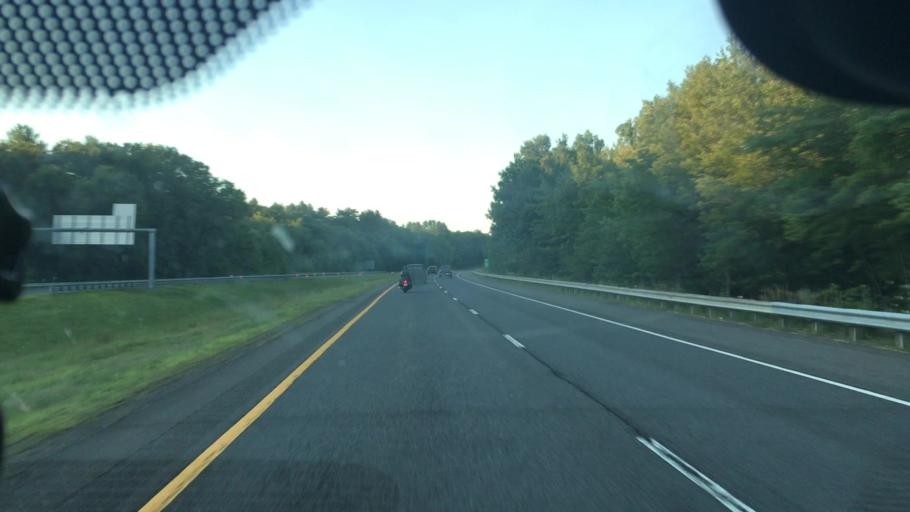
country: US
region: Massachusetts
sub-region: Franklin County
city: Turners Falls
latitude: 42.6306
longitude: -72.5813
